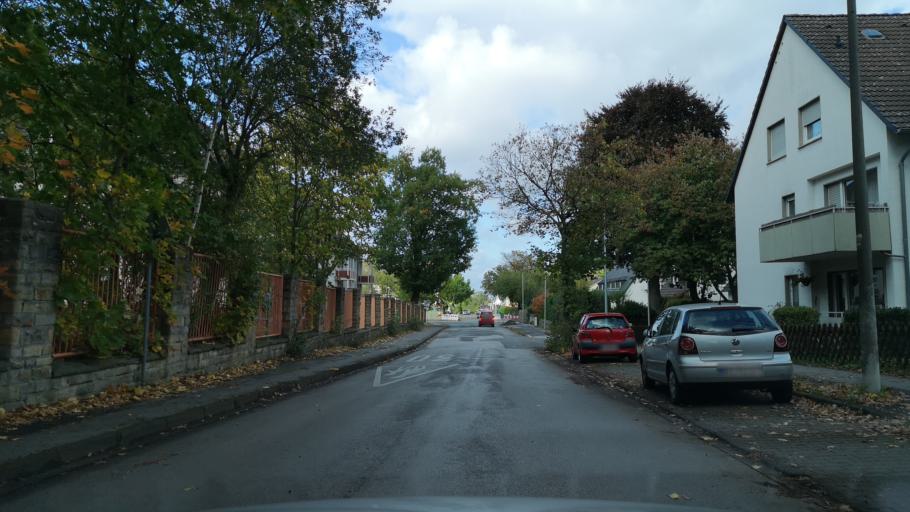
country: DE
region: North Rhine-Westphalia
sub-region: Regierungsbezirk Arnsberg
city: Menden
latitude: 51.4434
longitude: 7.7732
